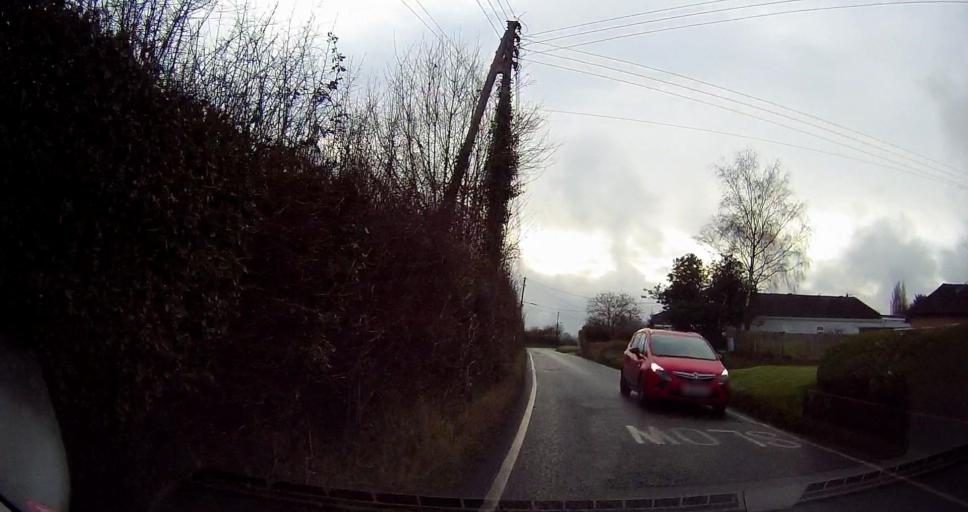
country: GB
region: England
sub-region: Greater London
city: Orpington
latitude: 51.3345
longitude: 0.0759
